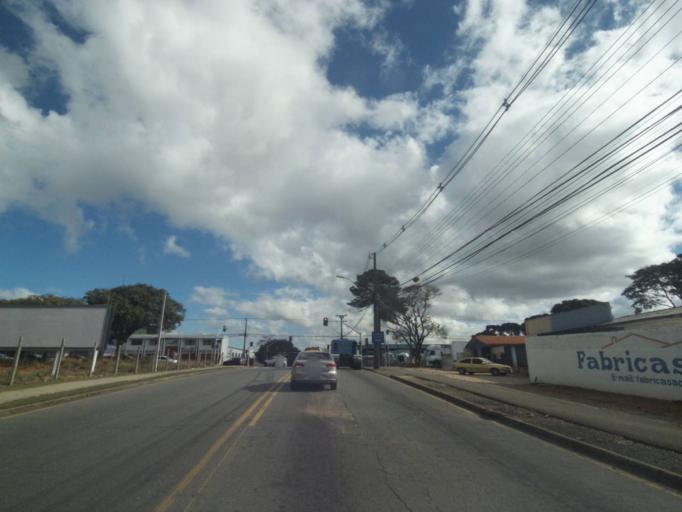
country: BR
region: Parana
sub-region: Sao Jose Dos Pinhais
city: Sao Jose dos Pinhais
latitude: -25.5319
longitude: -49.2970
